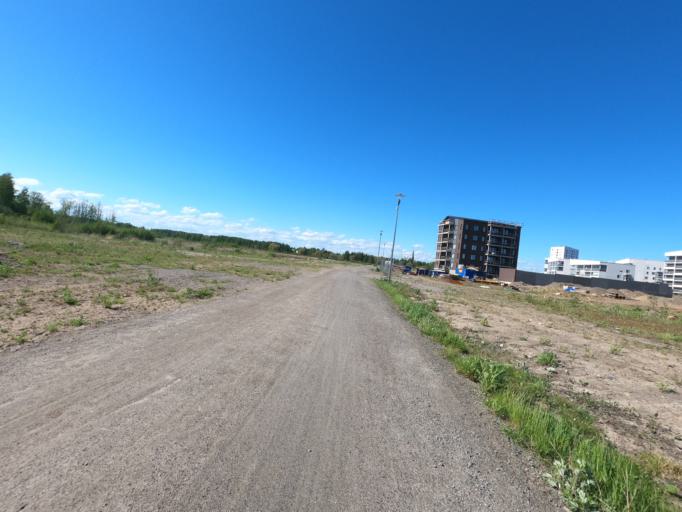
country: FI
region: North Karelia
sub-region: Joensuu
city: Joensuu
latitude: 62.5883
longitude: 29.7609
